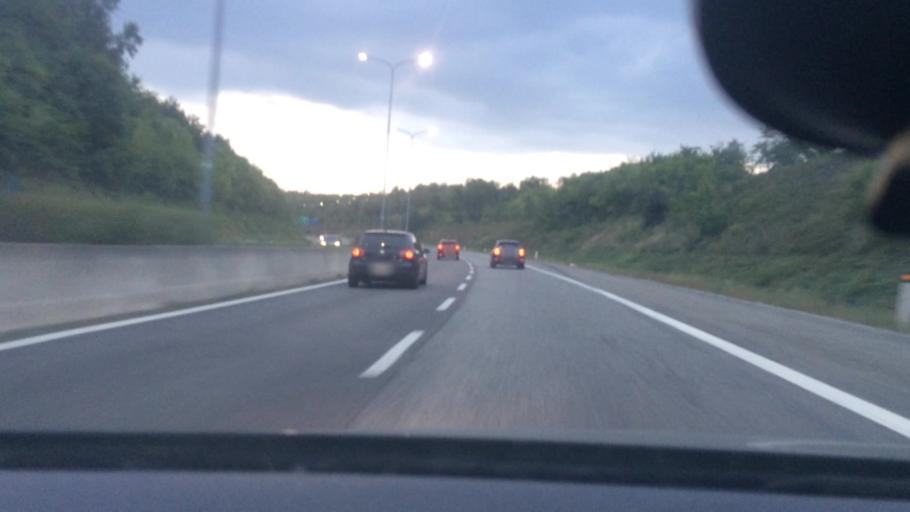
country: IT
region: Lombardy
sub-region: Provincia di Varese
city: Lonate Pozzolo
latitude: 45.5900
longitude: 8.7152
